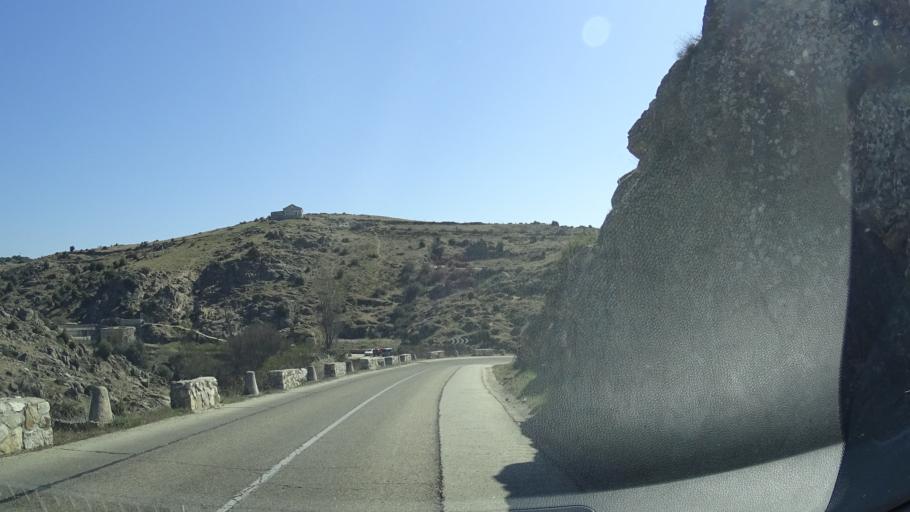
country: ES
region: Madrid
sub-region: Provincia de Madrid
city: Colmenar Viejo
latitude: 40.6488
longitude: -3.8096
